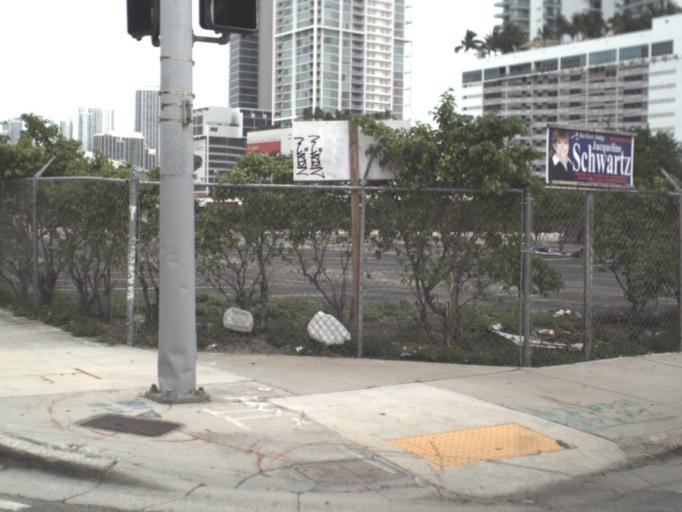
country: US
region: Florida
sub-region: Miami-Dade County
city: Miami
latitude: 25.7819
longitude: -80.1922
